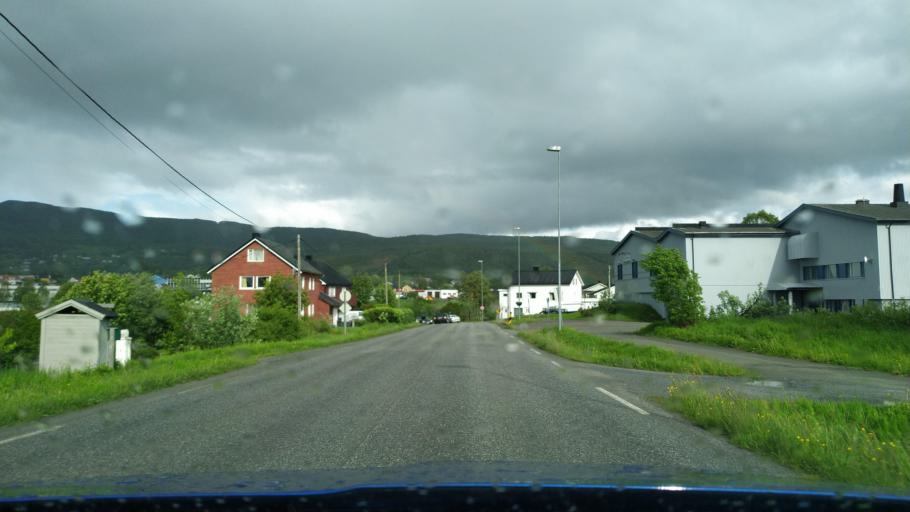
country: NO
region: Troms
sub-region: Sorreisa
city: Sorreisa
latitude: 69.1439
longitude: 18.1457
